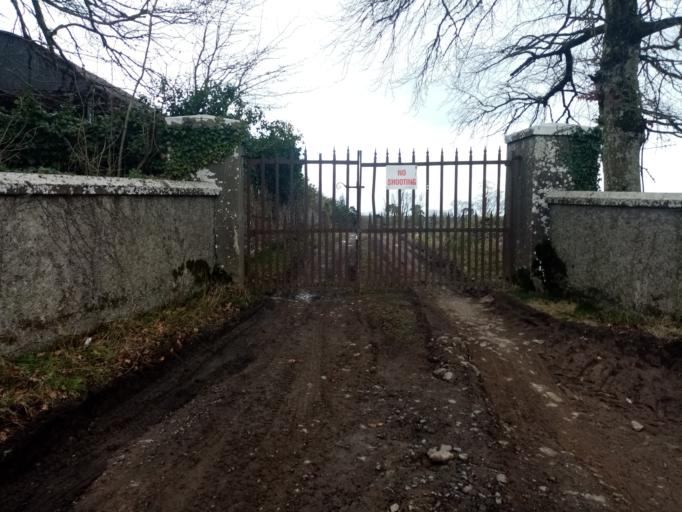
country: IE
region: Munster
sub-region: North Tipperary
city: Templemore
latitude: 52.7429
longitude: -7.9624
